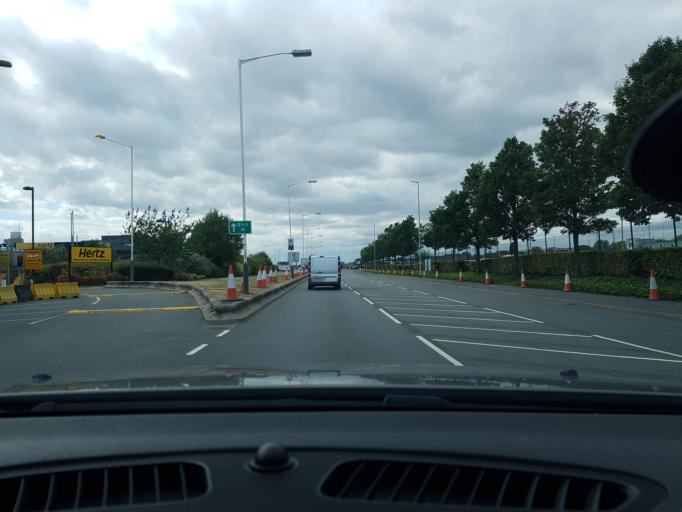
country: GB
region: England
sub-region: Greater London
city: West Drayton
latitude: 51.4799
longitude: -0.4741
